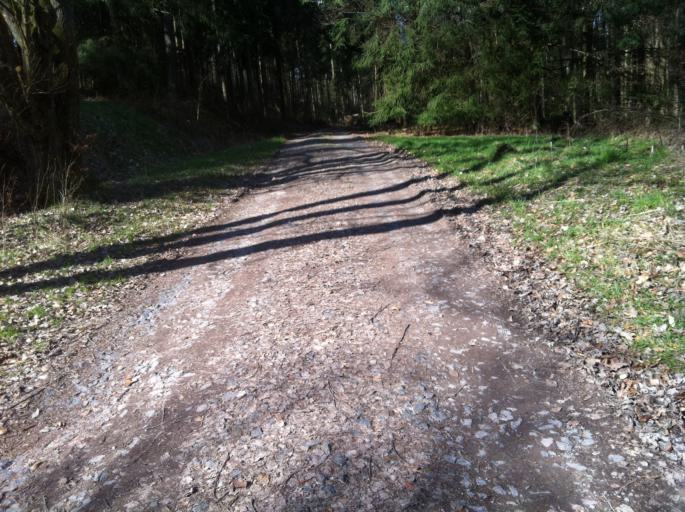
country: DE
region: Hesse
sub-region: Regierungsbezirk Darmstadt
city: Erbach
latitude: 49.6542
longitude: 8.9791
